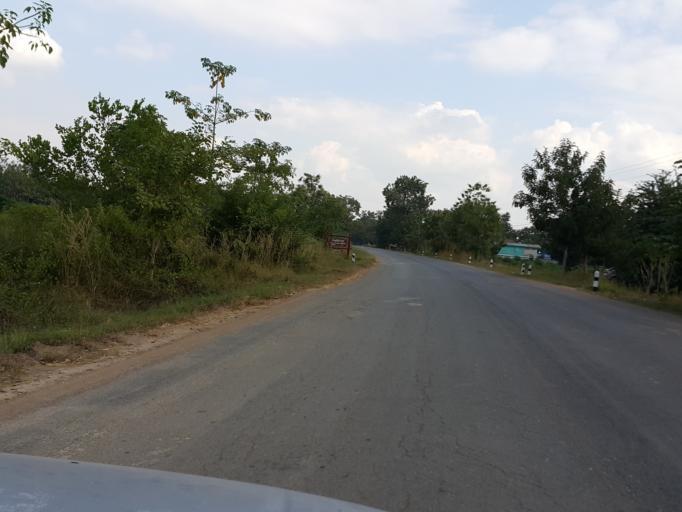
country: TH
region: Sukhothai
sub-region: Amphoe Si Satchanalai
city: Si Satchanalai
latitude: 17.4586
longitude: 99.6691
